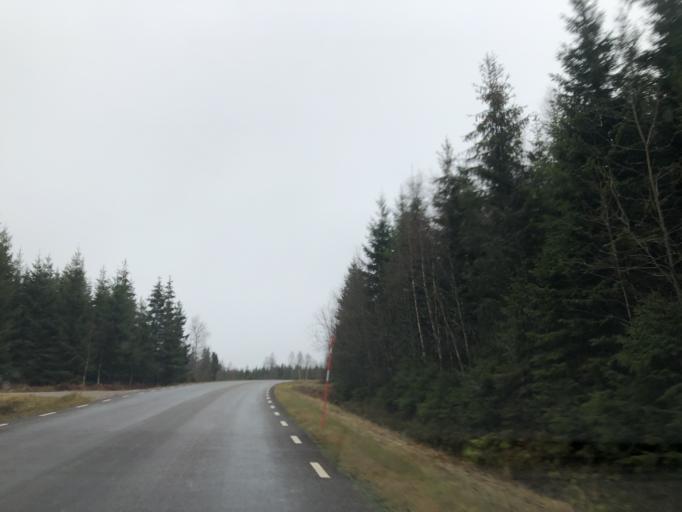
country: SE
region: Vaestra Goetaland
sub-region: Ulricehamns Kommun
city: Ulricehamn
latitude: 57.7203
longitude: 13.5550
